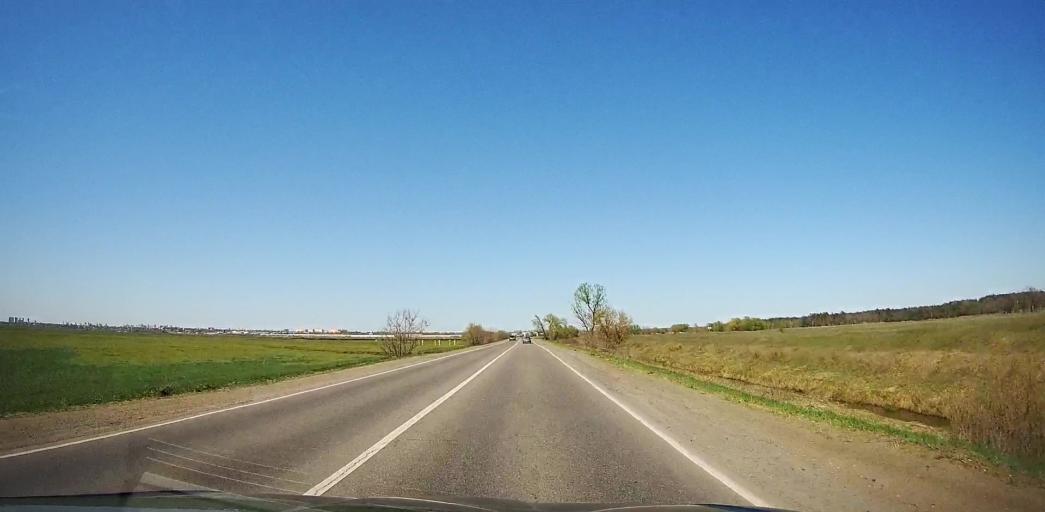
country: RU
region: Moskovskaya
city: Ramenskoye
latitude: 55.5223
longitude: 38.2768
